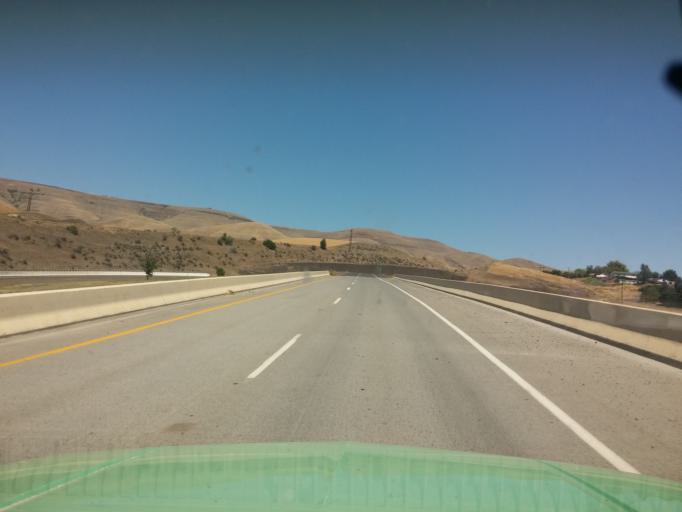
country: US
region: Idaho
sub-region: Nez Perce County
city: Lewiston
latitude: 46.4300
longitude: -116.9947
